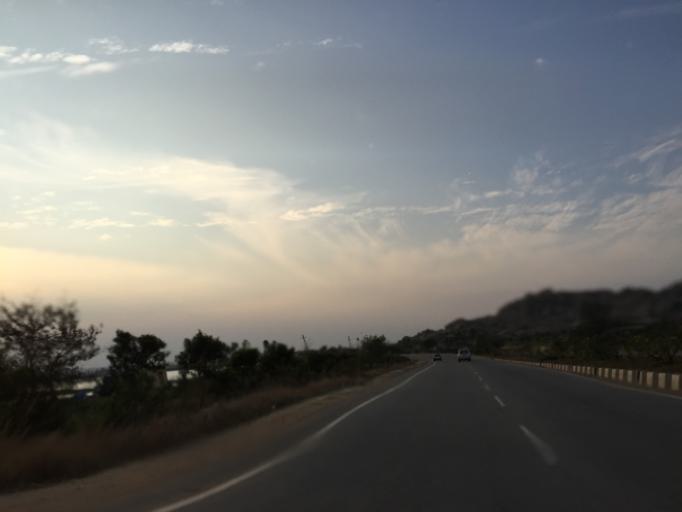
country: IN
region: Karnataka
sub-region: Kolar
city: Kolar
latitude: 13.1337
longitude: 78.0207
